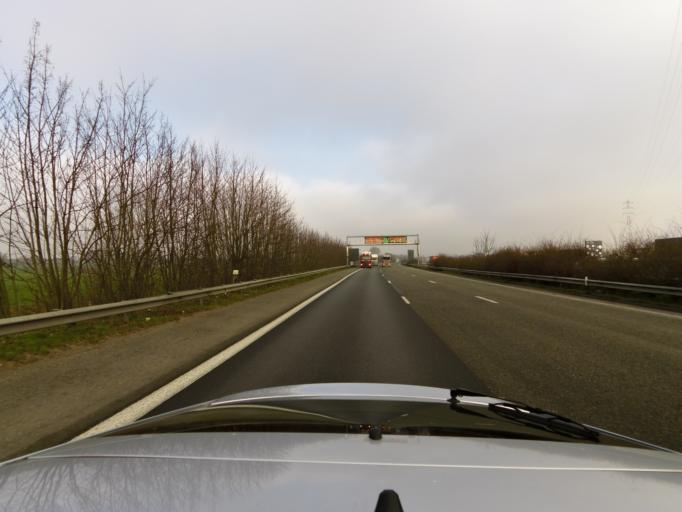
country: BE
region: Flanders
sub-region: Provincie West-Vlaanderen
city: Wevelgem
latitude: 50.8434
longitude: 3.1752
